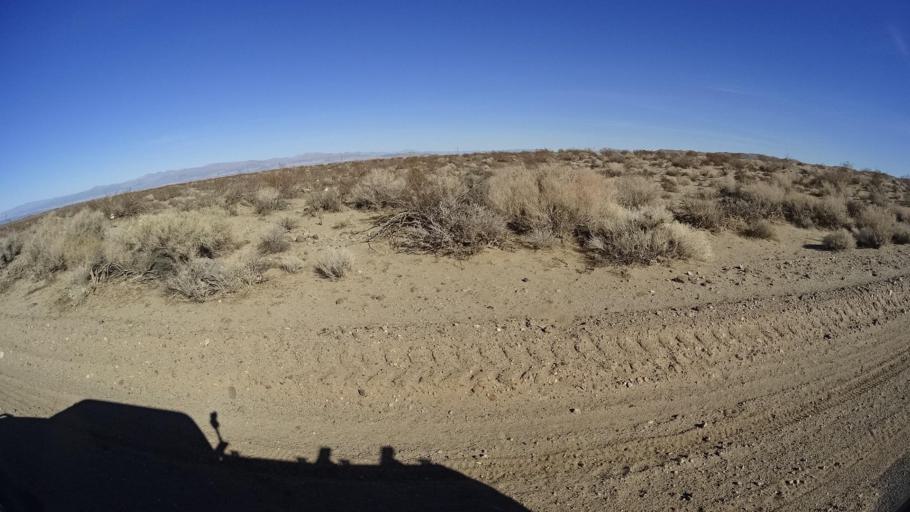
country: US
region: California
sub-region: Kern County
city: China Lake Acres
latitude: 35.5720
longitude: -117.7819
